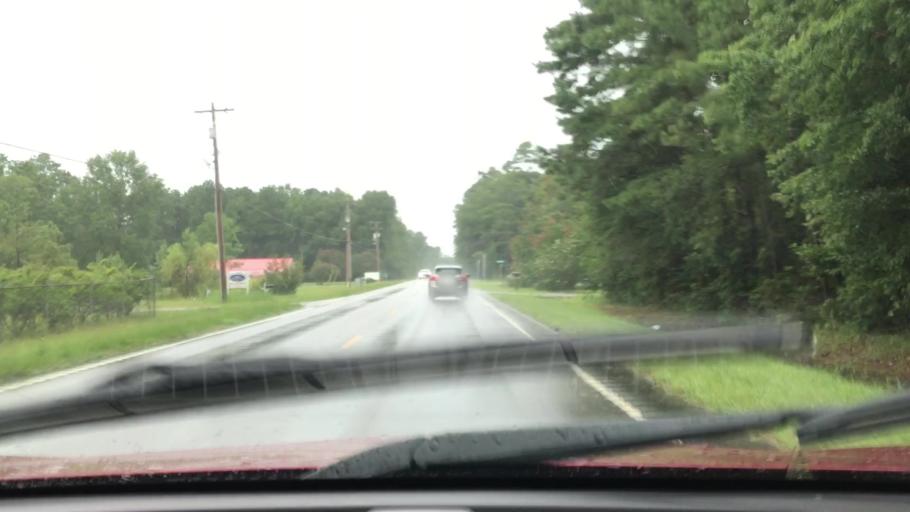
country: US
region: South Carolina
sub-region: Horry County
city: Conway
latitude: 33.7856
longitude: -79.0752
